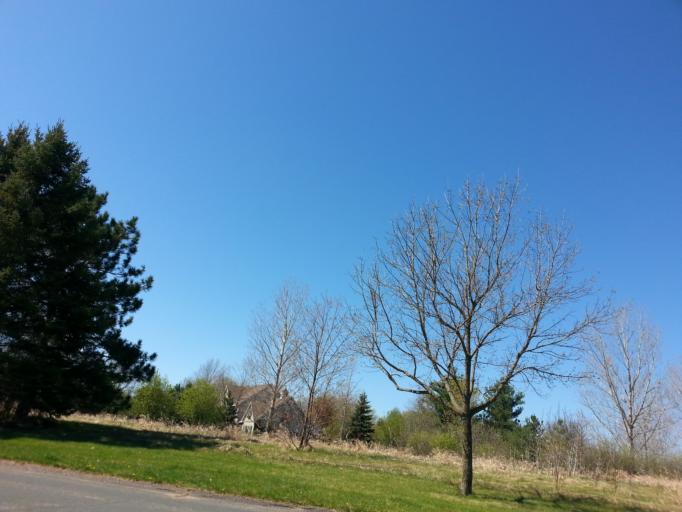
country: US
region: Minnesota
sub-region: Washington County
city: Lake Elmo
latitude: 44.9584
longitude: -92.8293
